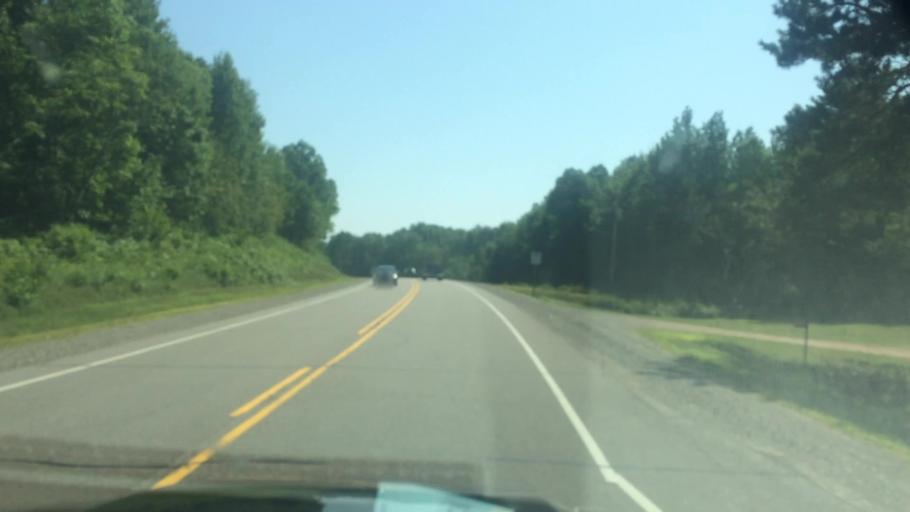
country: US
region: Wisconsin
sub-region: Lincoln County
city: Tomahawk
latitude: 45.5676
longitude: -89.6216
